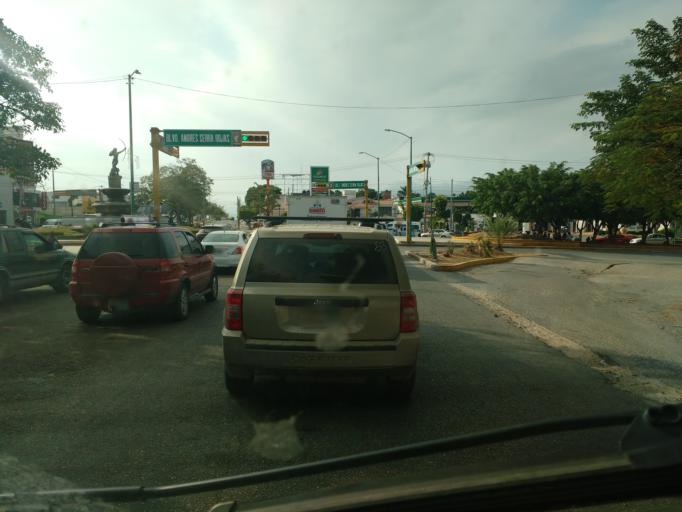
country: MX
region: Chiapas
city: Tuxtla Gutierrez
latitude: 16.7476
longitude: -93.0827
